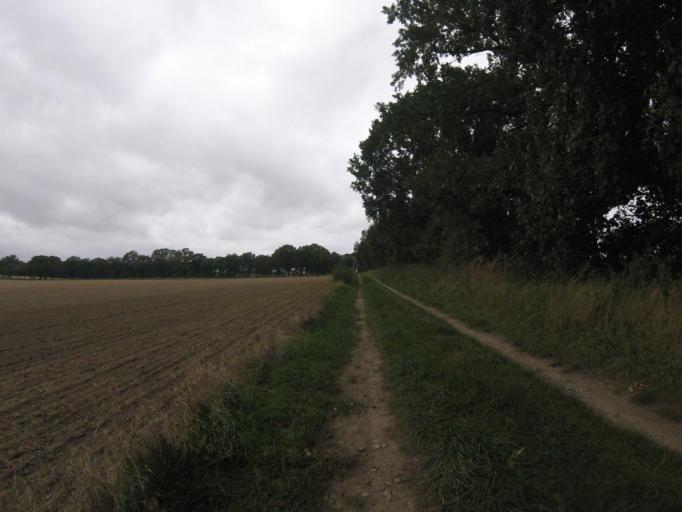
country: DE
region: Brandenburg
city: Mittenwalde
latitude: 52.2912
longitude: 13.5734
